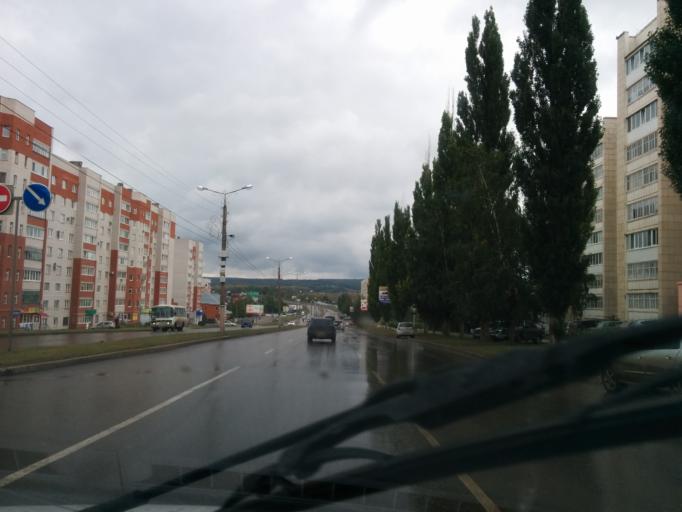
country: RU
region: Bashkortostan
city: Oktyabr'skiy
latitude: 54.4817
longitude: 53.5196
